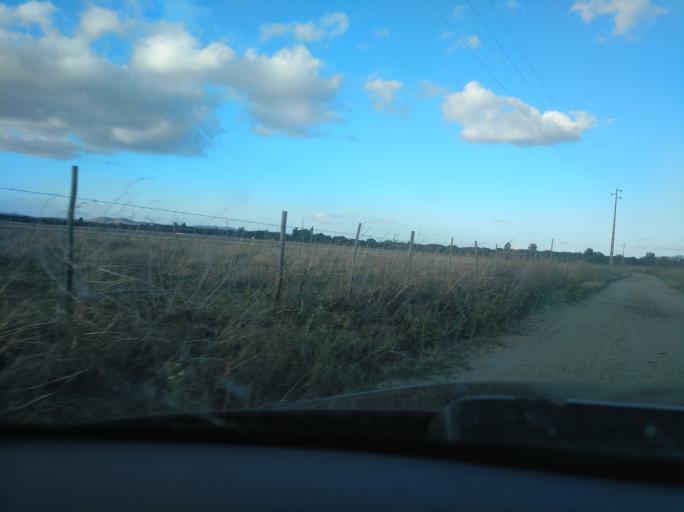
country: PT
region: Portalegre
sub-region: Campo Maior
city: Campo Maior
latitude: 39.0386
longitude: -6.9800
